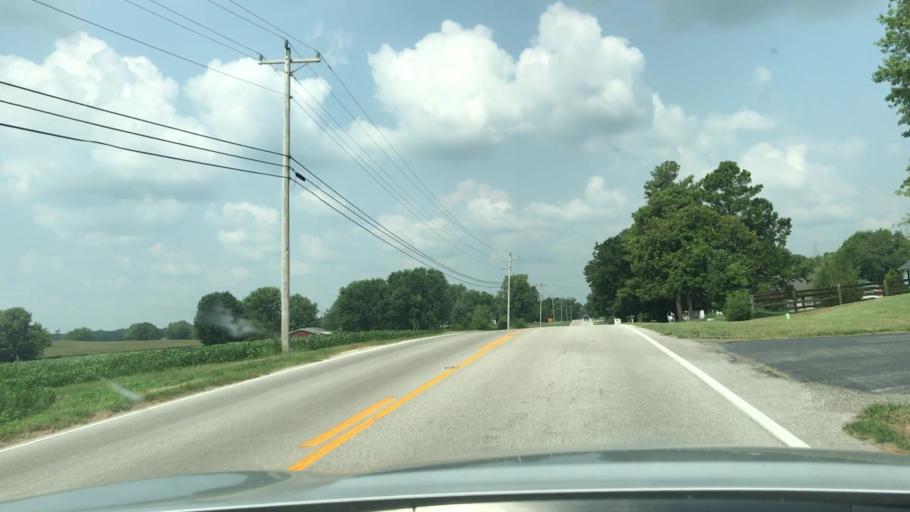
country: US
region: Kentucky
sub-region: Todd County
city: Elkton
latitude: 36.8053
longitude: -87.1272
